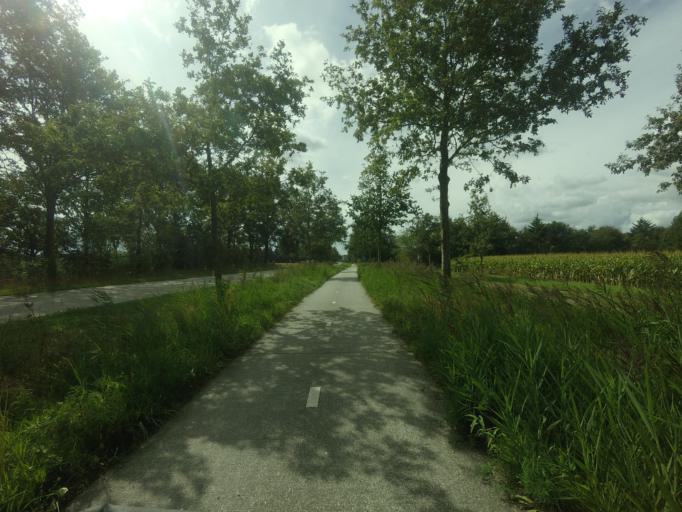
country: NL
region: Groningen
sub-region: Gemeente Leek
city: Leek
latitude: 53.0316
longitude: 6.4200
